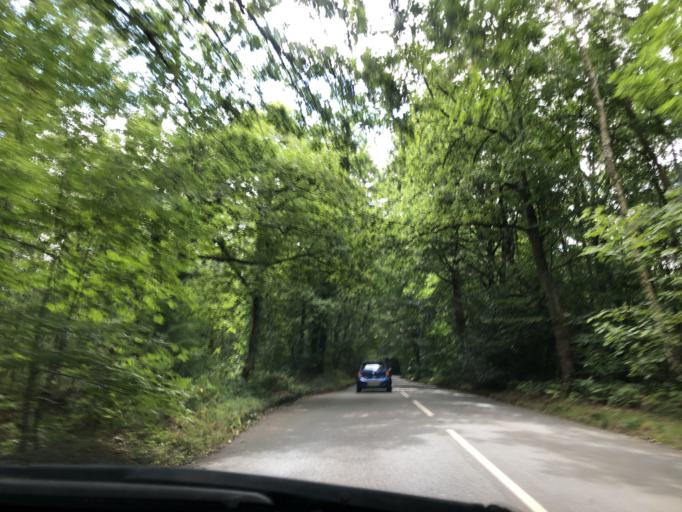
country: GB
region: England
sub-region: Kent
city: Westerham
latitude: 51.2555
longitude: 0.0796
